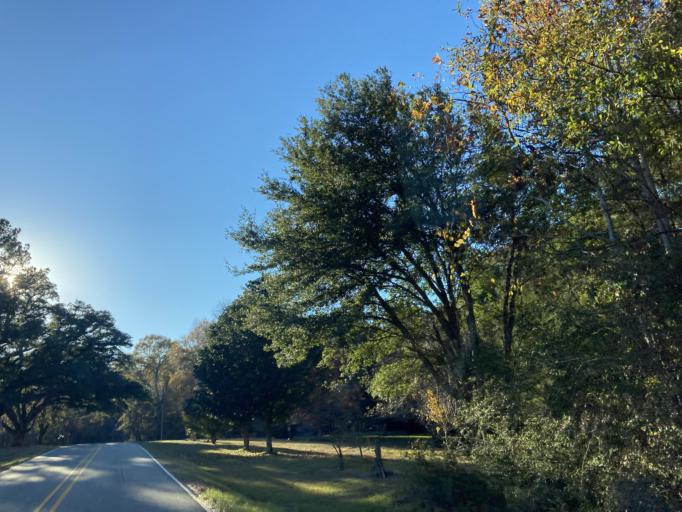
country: US
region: Mississippi
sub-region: Lamar County
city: Sumrall
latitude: 31.3315
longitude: -89.5817
